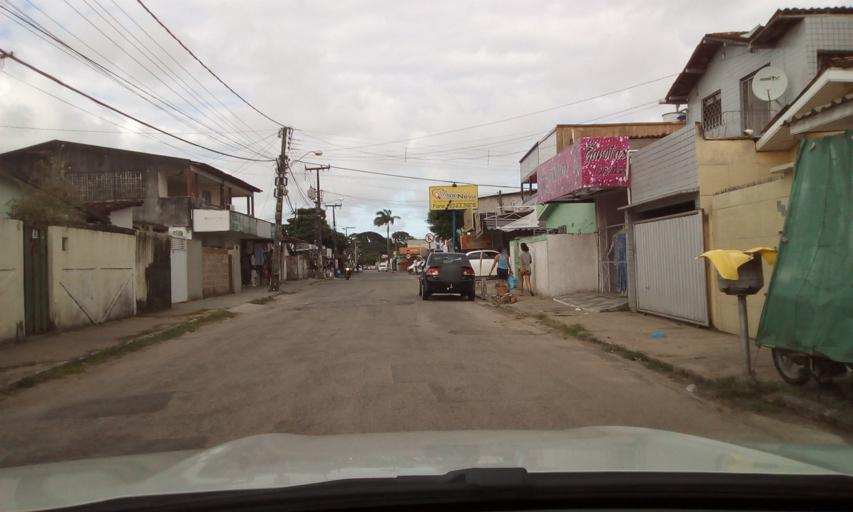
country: BR
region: Paraiba
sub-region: Joao Pessoa
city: Joao Pessoa
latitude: -7.1503
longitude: -34.8743
